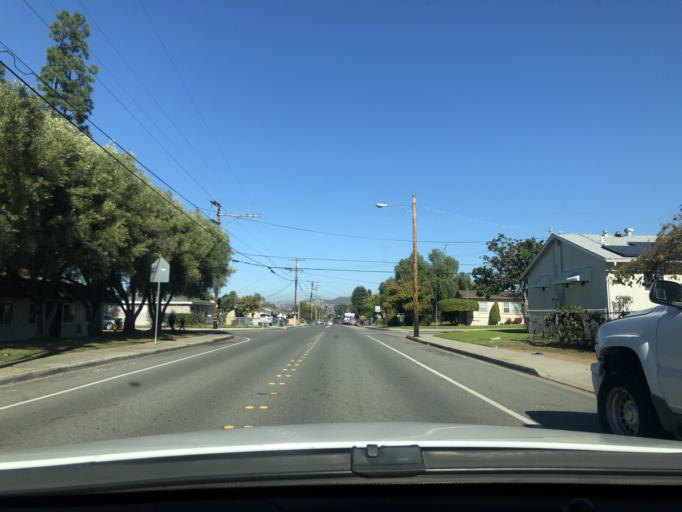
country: US
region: California
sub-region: San Diego County
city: El Cajon
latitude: 32.7843
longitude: -116.9482
